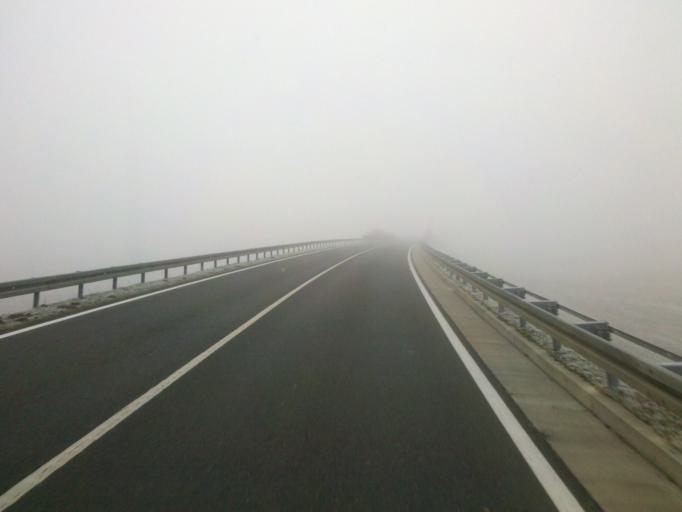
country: HR
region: Varazdinska
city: Jalkovec
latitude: 46.2847
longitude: 16.3108
